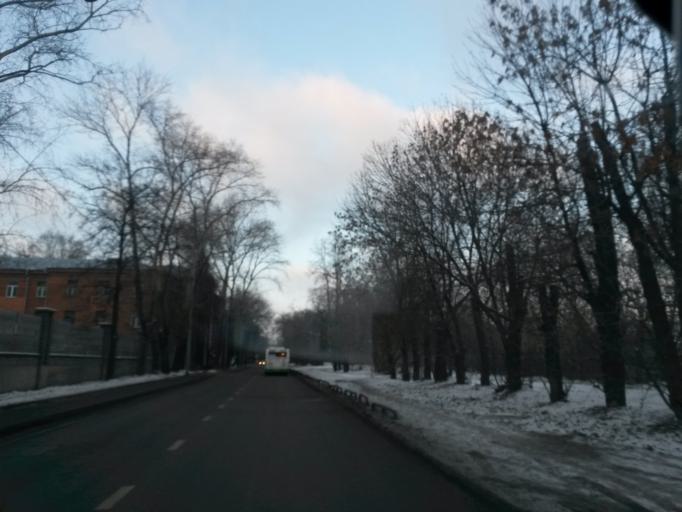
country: RU
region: Moscow
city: Amin'yevo
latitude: 55.7115
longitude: 37.4436
